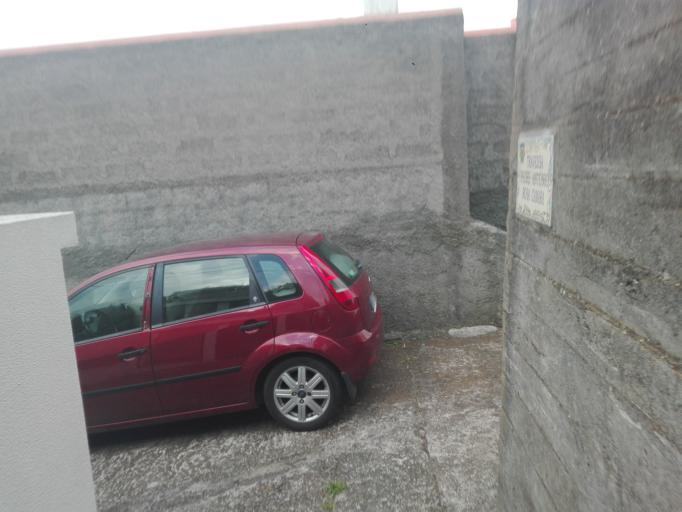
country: PT
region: Madeira
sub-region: Santa Cruz
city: Camacha
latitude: 32.6549
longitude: -16.8261
